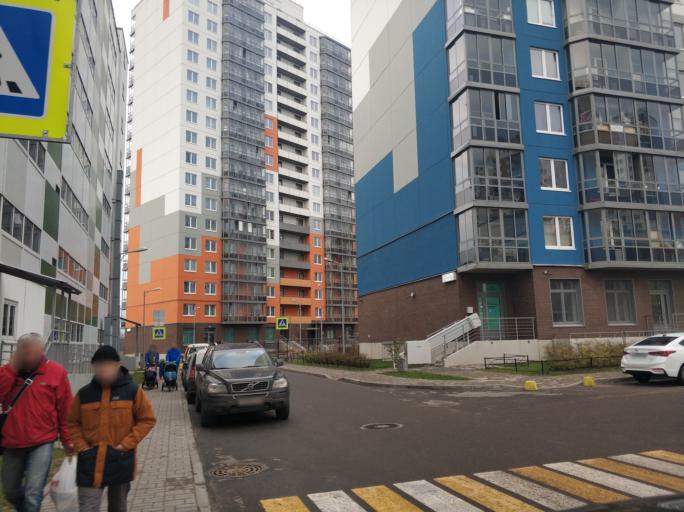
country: RU
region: Leningrad
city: Murino
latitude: 60.0535
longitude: 30.4498
